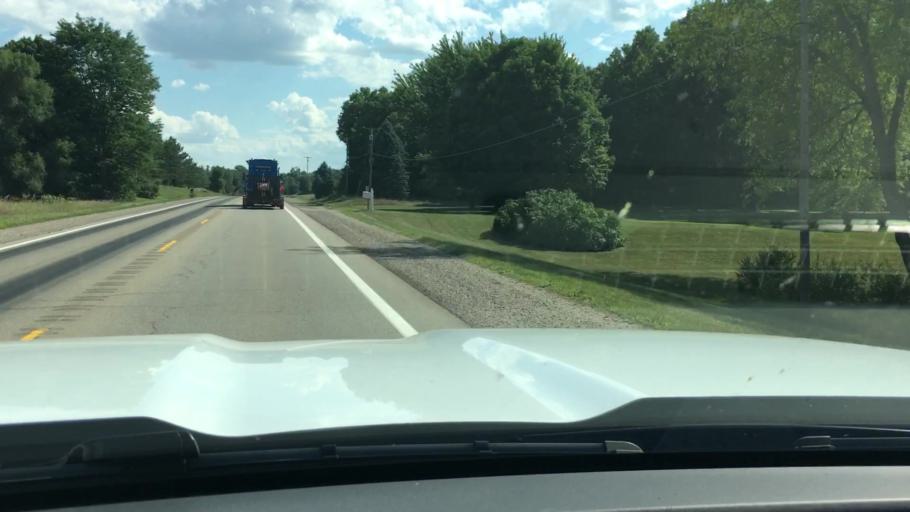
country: US
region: Michigan
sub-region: Ionia County
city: Ionia
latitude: 43.1100
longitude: -85.0751
